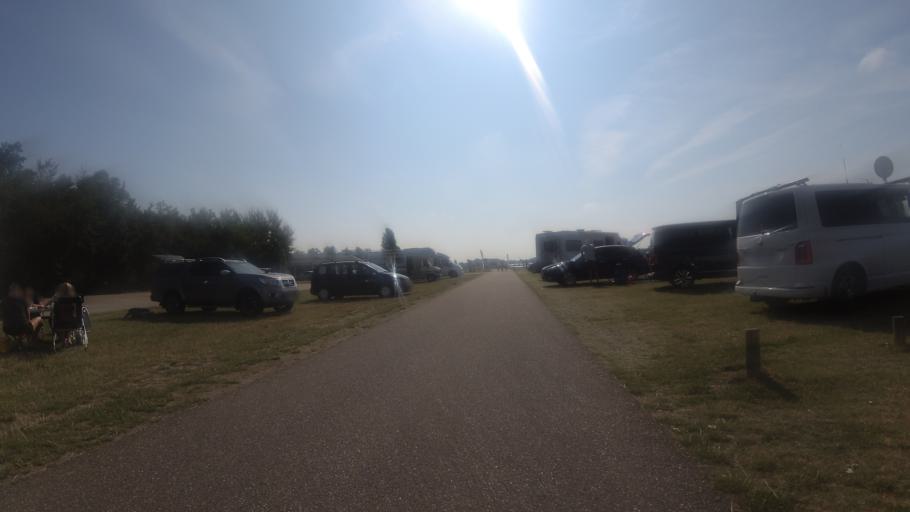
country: NL
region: Zeeland
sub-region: Gemeente Veere
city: Veere
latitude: 51.5695
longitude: 3.6553
